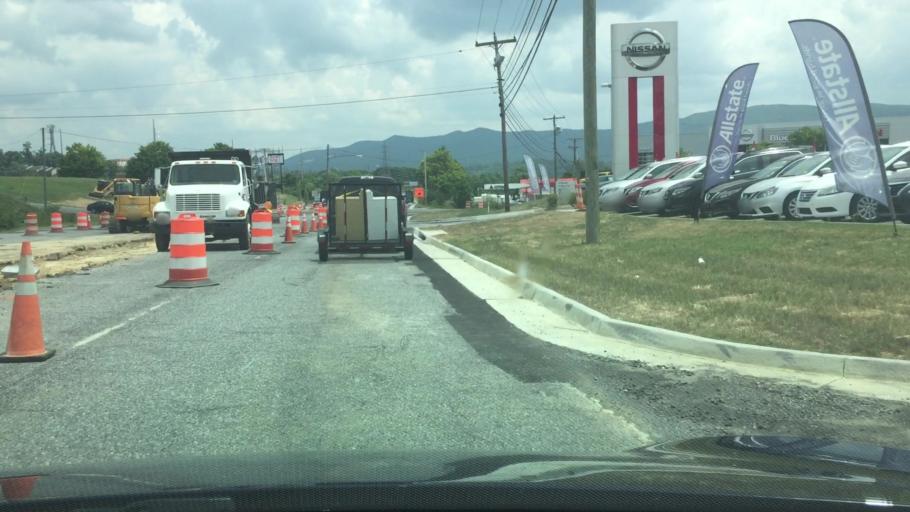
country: US
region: Virginia
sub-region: Wythe County
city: Wytheville
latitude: 36.9507
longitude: -81.0677
